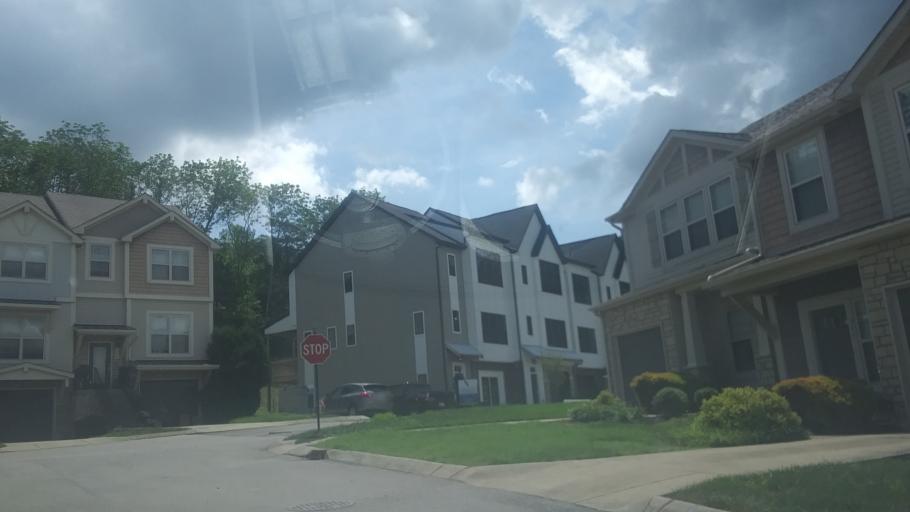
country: US
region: Tennessee
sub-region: Davidson County
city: Belle Meade
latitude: 36.1114
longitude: -86.9182
